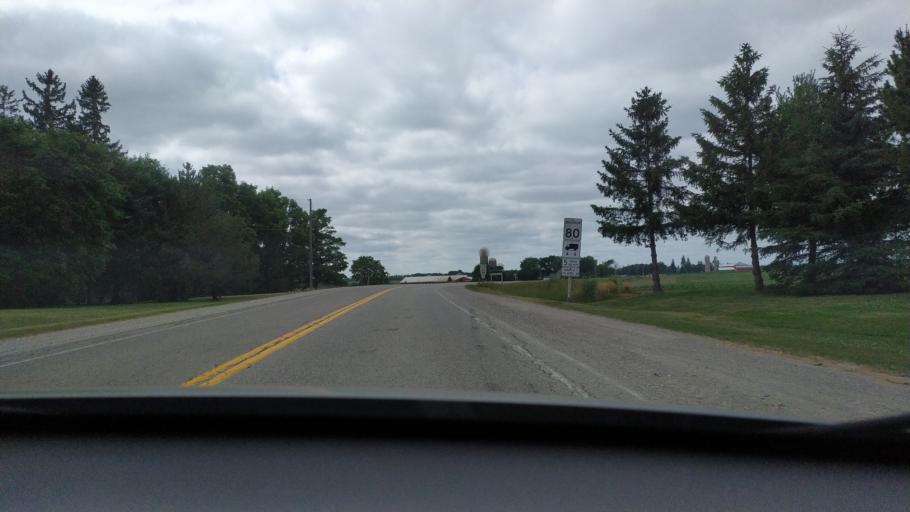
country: CA
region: Ontario
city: Stratford
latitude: 43.2824
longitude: -80.9648
